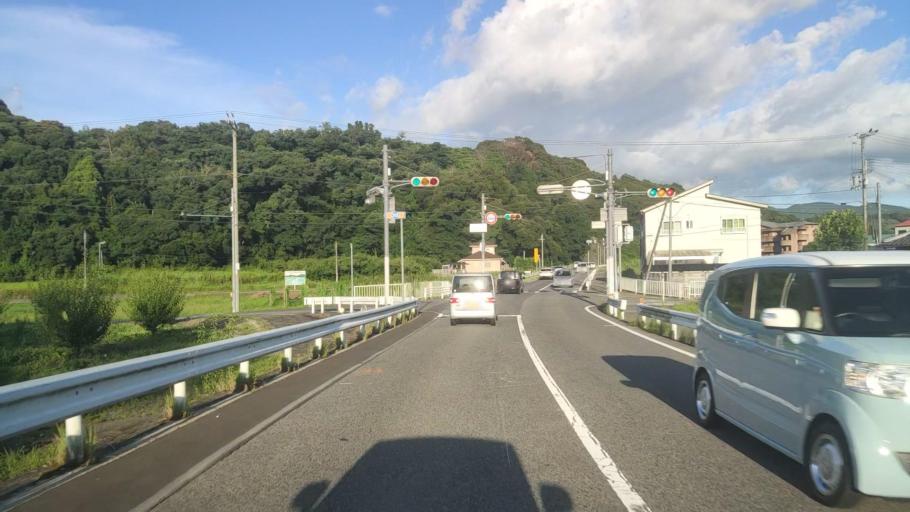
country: JP
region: Wakayama
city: Tanabe
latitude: 33.7266
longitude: 135.4418
